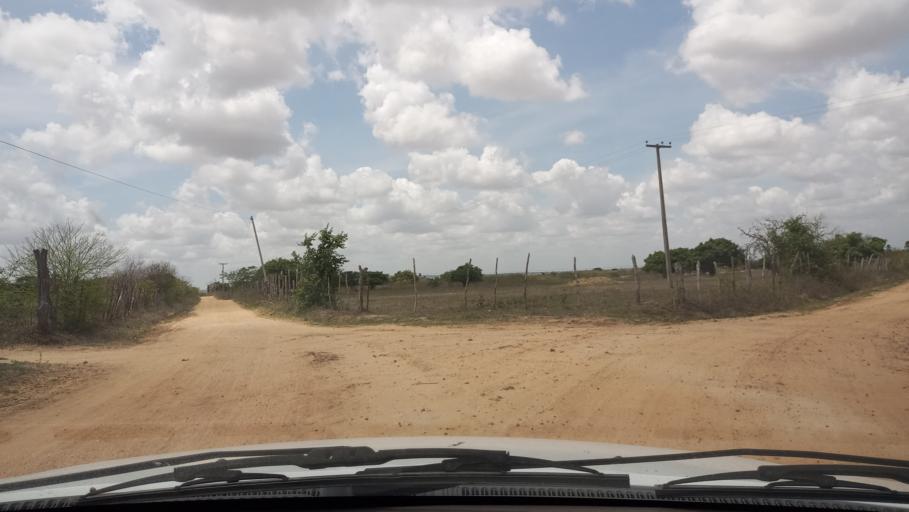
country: BR
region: Rio Grande do Norte
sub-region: Brejinho
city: Brejinho
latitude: -6.2767
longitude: -35.3474
